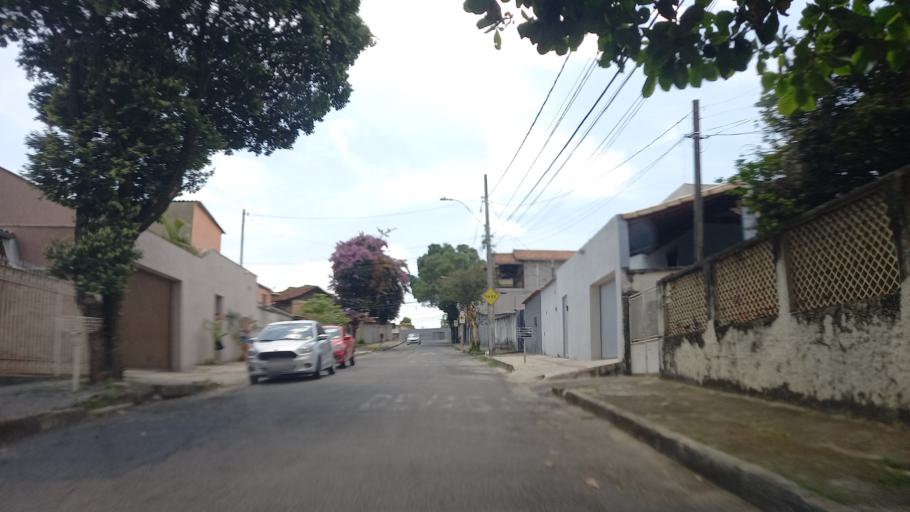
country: BR
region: Minas Gerais
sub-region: Contagem
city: Contagem
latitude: -19.9076
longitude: -44.0064
